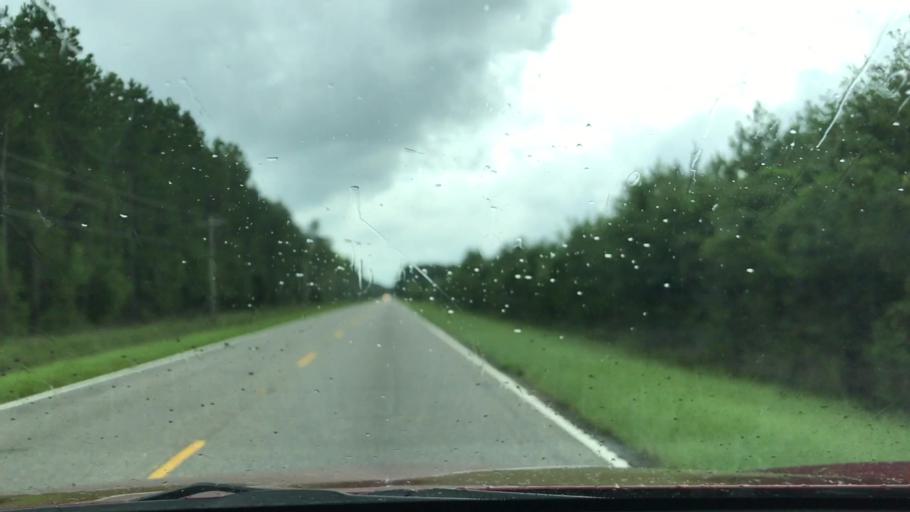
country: US
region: South Carolina
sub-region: Georgetown County
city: Georgetown
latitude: 33.5130
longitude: -79.2506
